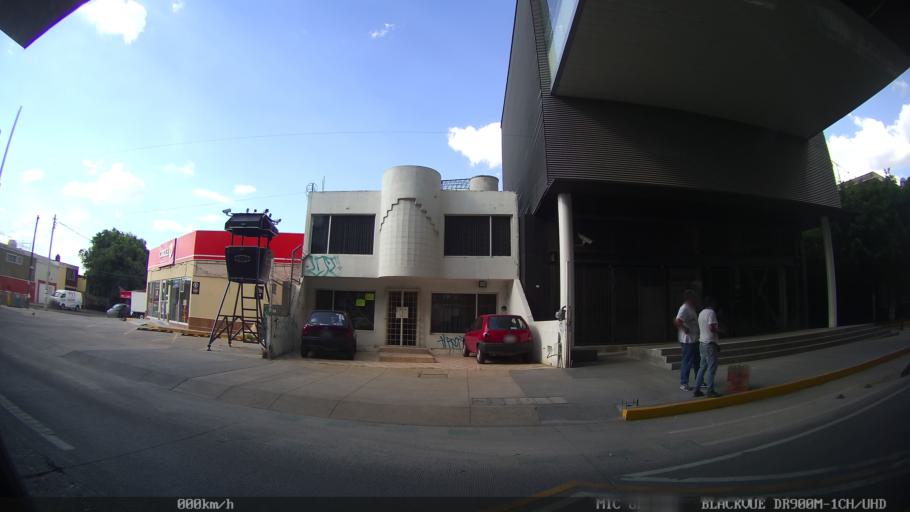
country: MX
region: Jalisco
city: Tlaquepaque
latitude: 20.6595
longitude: -103.3236
